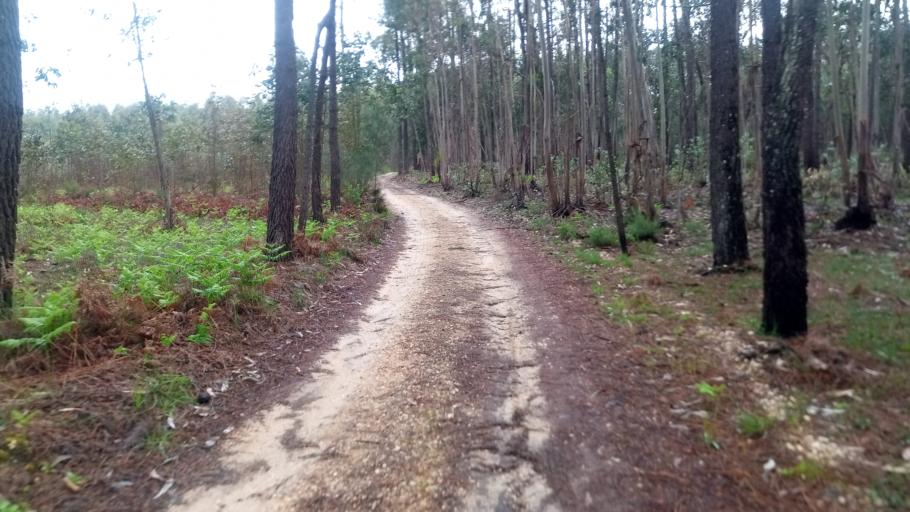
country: PT
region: Leiria
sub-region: Caldas da Rainha
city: Caldas da Rainha
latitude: 39.4339
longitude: -9.1674
